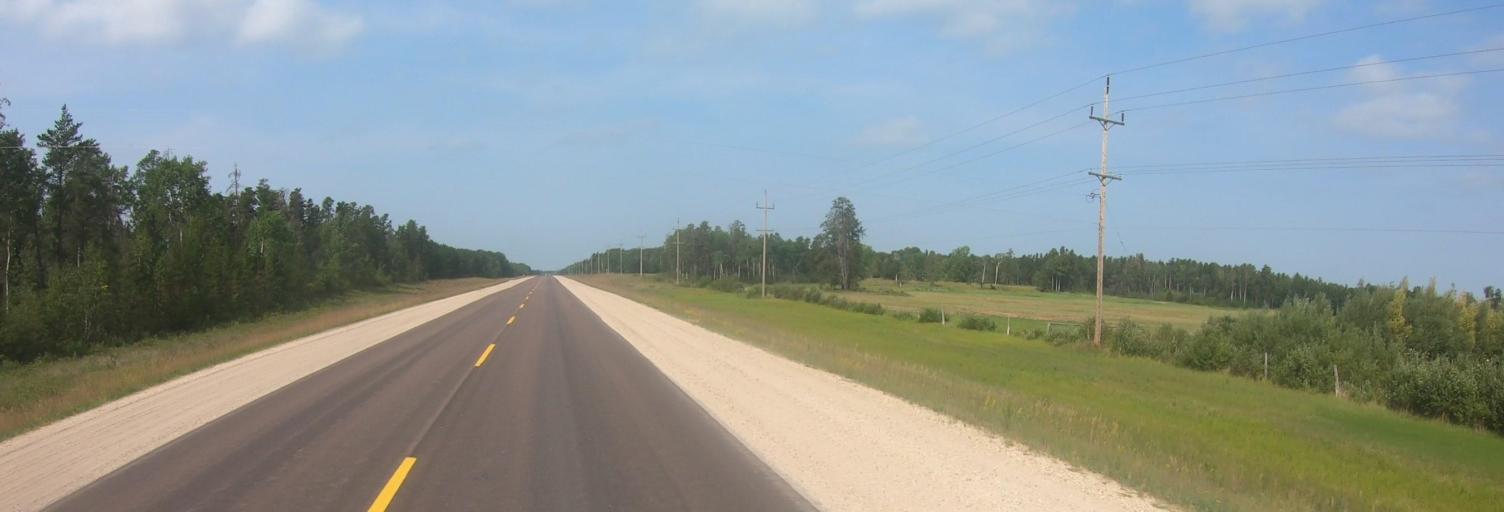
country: CA
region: Manitoba
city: La Broquerie
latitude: 49.2668
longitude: -96.4298
